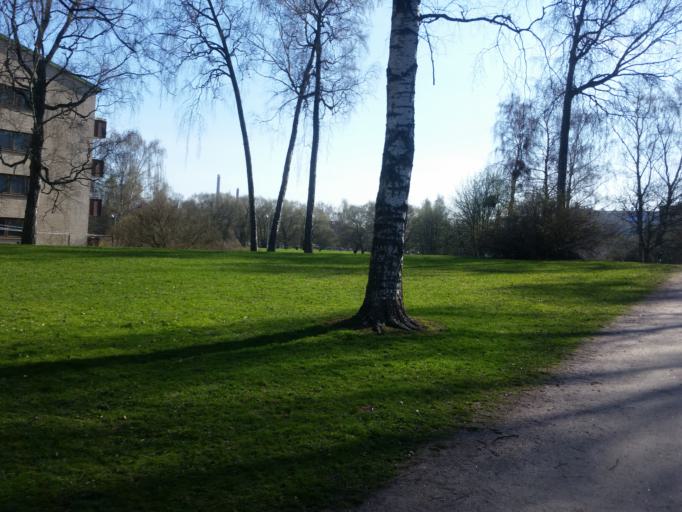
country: FI
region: Uusimaa
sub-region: Helsinki
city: Teekkarikylae
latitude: 60.1558
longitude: 24.8800
